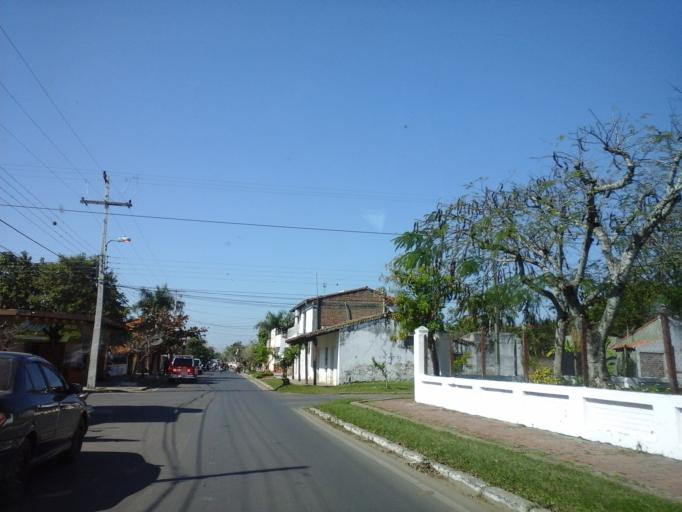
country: PY
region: Neembucu
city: Pilar
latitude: -26.8596
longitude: -58.3035
